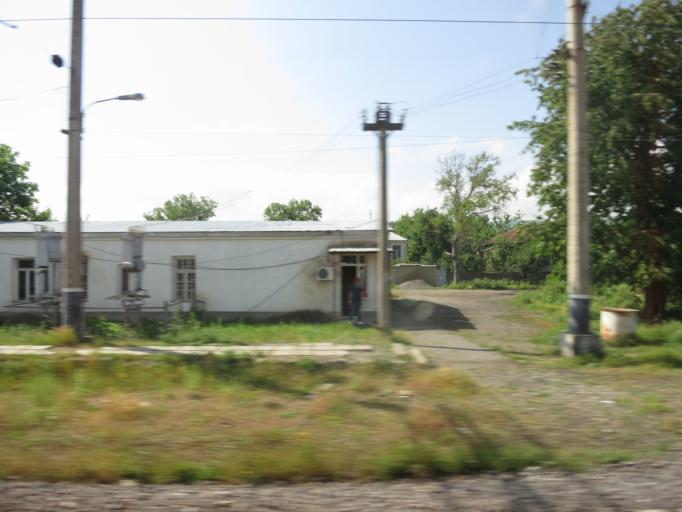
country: GE
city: Agara
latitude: 42.0197
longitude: 43.7249
